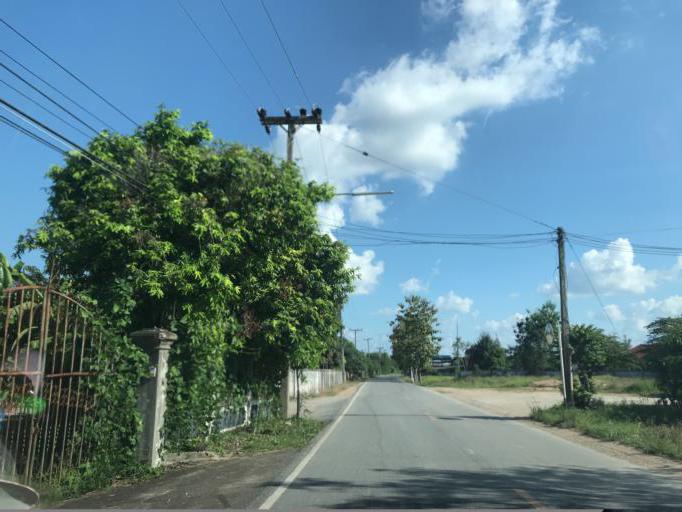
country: TH
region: Chiang Mai
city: Doi Lo
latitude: 18.5364
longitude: 98.8396
